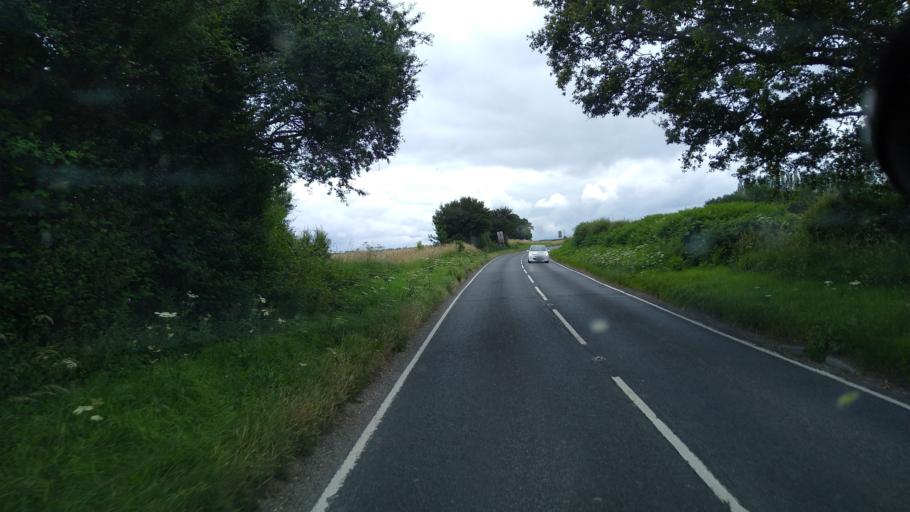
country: GB
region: England
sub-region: Hampshire
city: Alton
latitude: 51.1265
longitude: -0.9540
